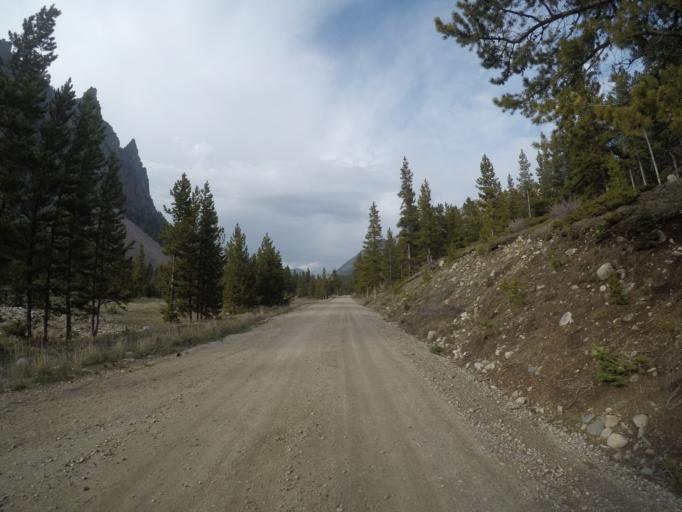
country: US
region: Montana
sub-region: Carbon County
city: Red Lodge
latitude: 45.0280
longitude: -109.4374
